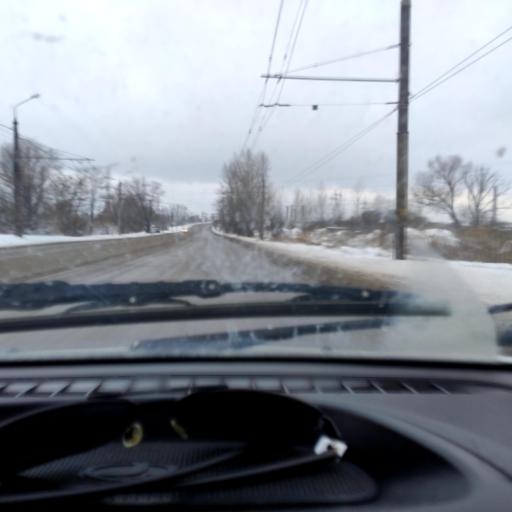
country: RU
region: Samara
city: Zhigulevsk
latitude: 53.4932
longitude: 49.5043
